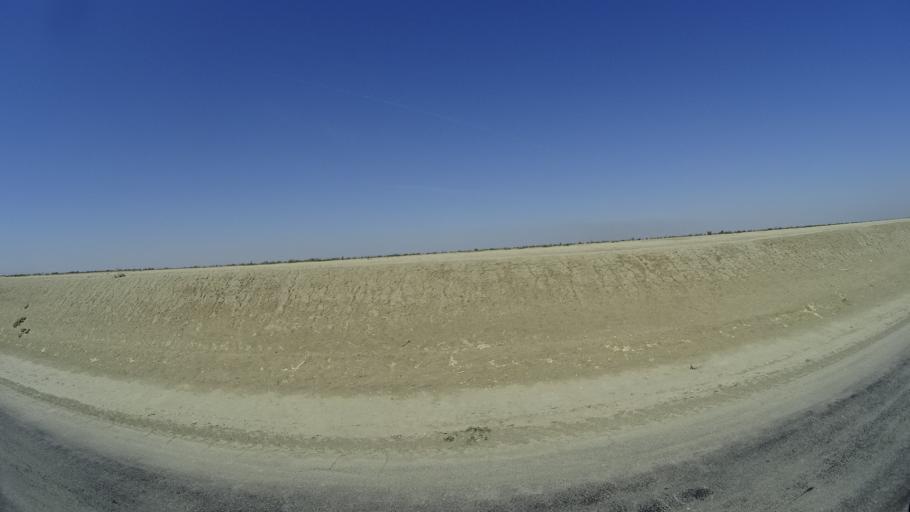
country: US
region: California
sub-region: Kings County
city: Corcoran
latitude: 36.0167
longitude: -119.5361
